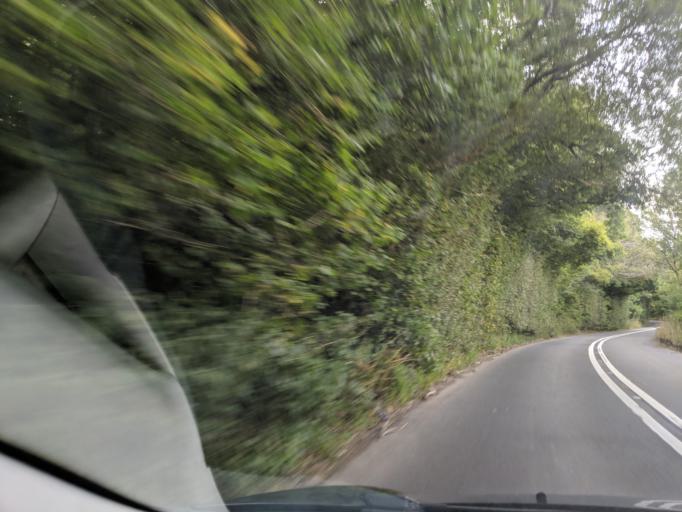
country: GB
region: England
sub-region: Devon
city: Winkleigh
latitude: 50.9501
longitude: -3.9276
